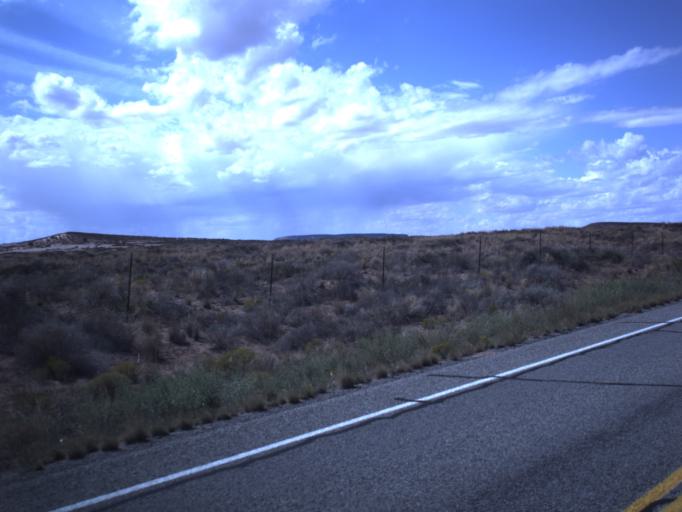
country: US
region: Utah
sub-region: San Juan County
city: Blanding
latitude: 37.2983
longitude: -109.4659
